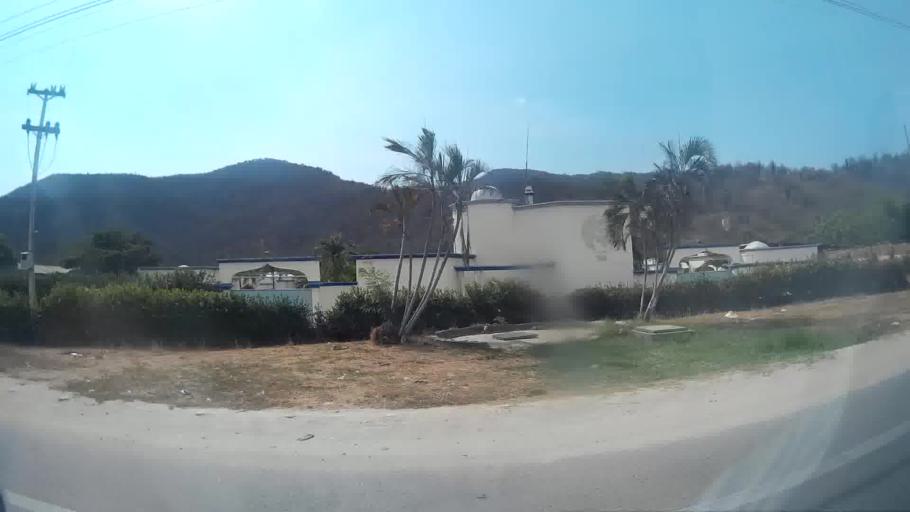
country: CO
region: Magdalena
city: Santa Marta
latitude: 11.1933
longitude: -74.2066
